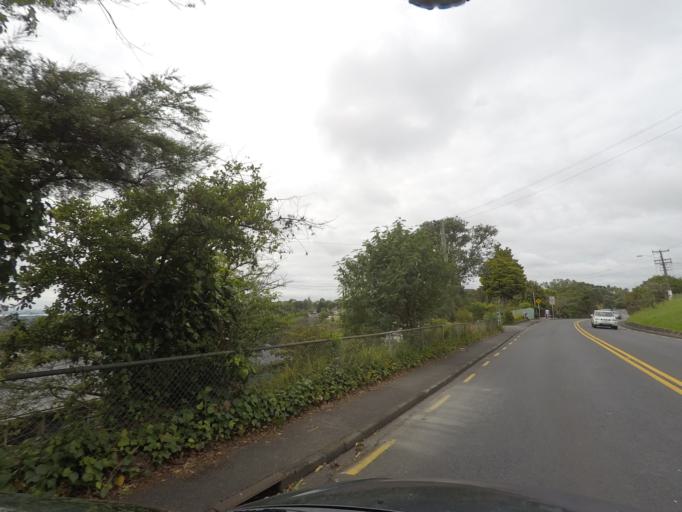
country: NZ
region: Auckland
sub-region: Auckland
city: Rosebank
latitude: -36.8385
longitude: 174.6004
